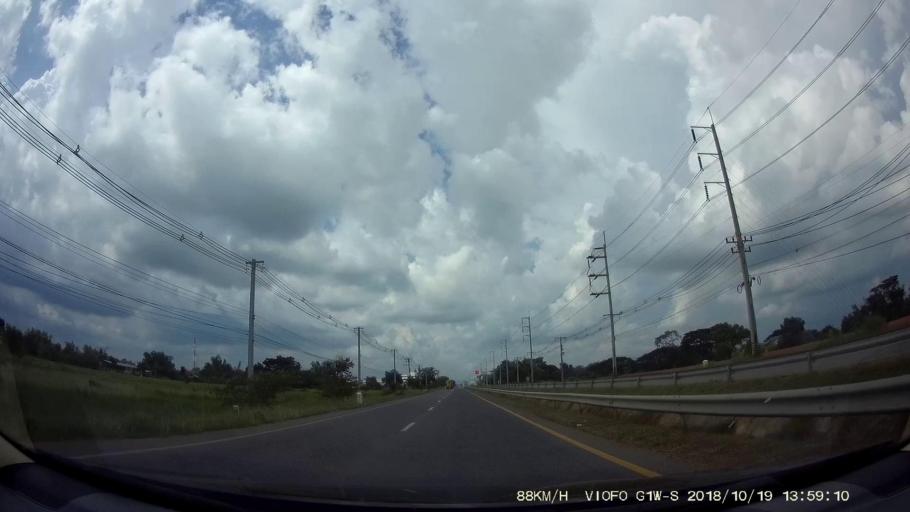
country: TH
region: Chaiyaphum
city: Chaiyaphum
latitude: 15.8058
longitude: 102.0612
